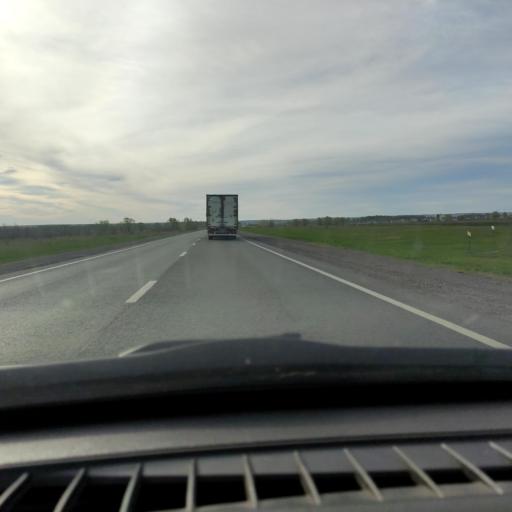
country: RU
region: Samara
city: Krasnyy Yar
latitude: 53.5125
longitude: 50.4140
